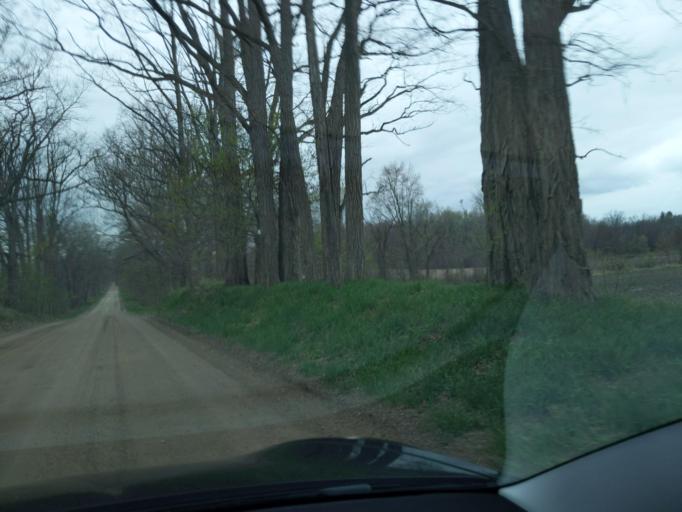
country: US
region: Michigan
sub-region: Ingham County
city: Stockbridge
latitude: 42.4462
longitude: -84.1214
